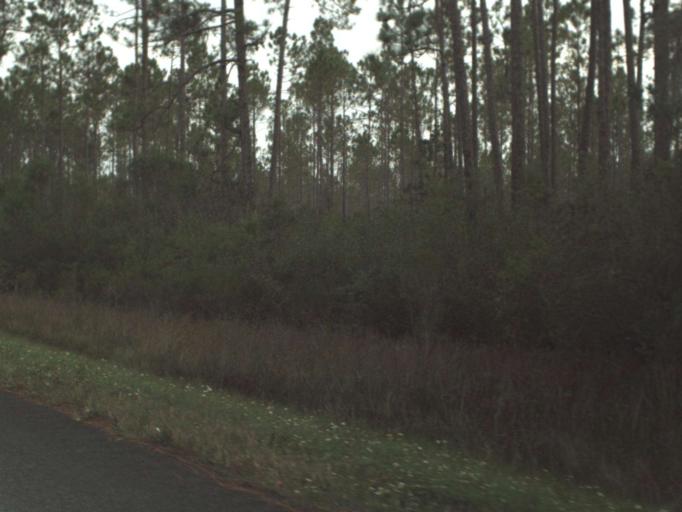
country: US
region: Florida
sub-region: Franklin County
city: Eastpoint
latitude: 29.8278
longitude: -84.9180
